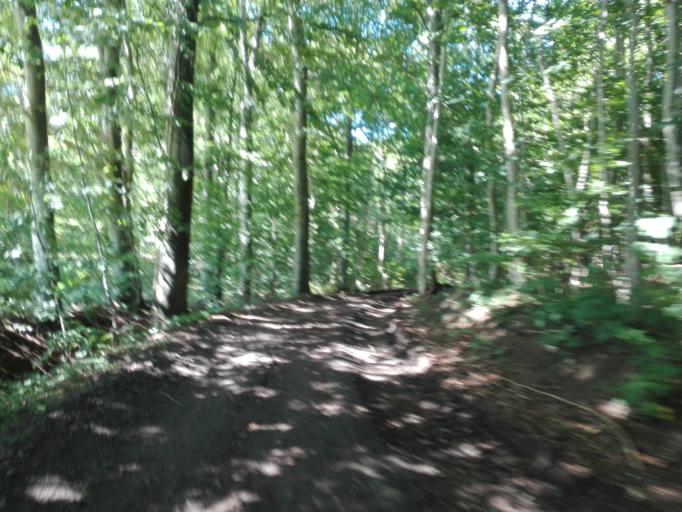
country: DK
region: Central Jutland
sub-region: Odder Kommune
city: Odder
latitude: 55.9491
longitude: 10.1479
